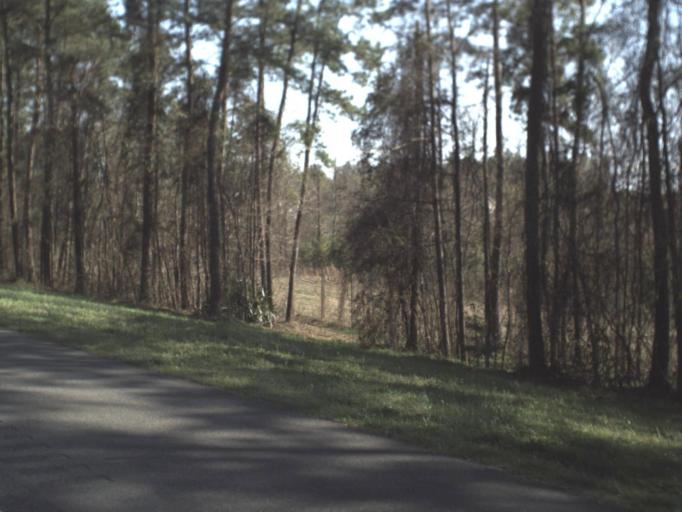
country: US
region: Florida
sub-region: Gadsden County
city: Midway
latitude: 30.5149
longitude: -84.4789
